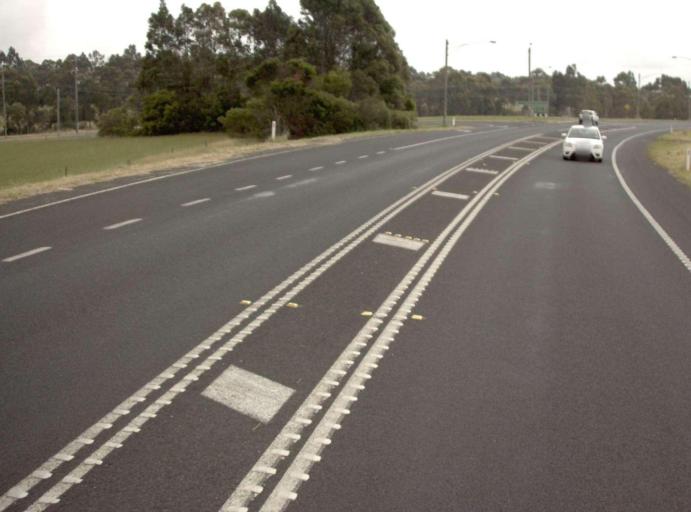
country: AU
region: Victoria
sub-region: Latrobe
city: Morwell
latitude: -38.2800
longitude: 146.4125
